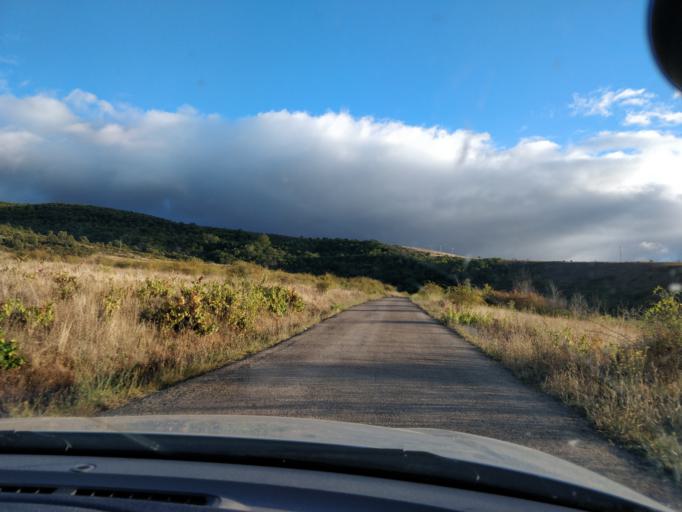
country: ES
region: Castille and Leon
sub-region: Provincia de Leon
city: Borrenes
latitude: 42.4881
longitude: -6.7018
